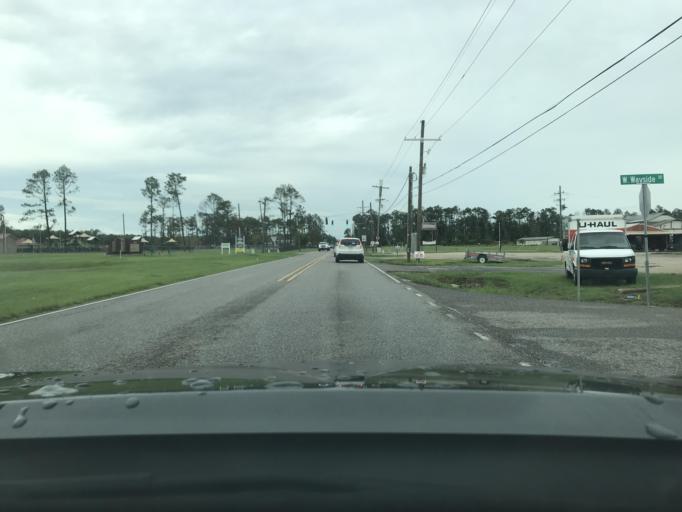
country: US
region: Louisiana
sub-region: Calcasieu Parish
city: Westlake
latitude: 30.2742
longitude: -93.2582
